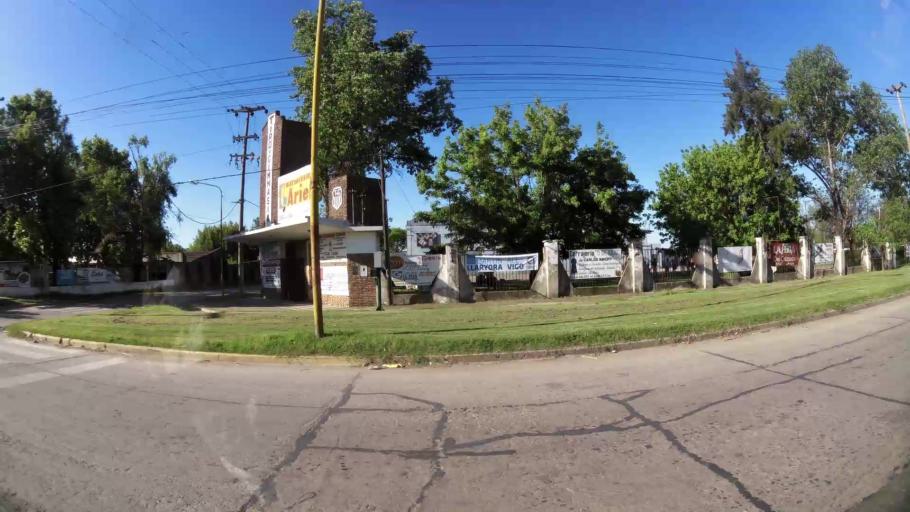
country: AR
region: Cordoba
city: San Francisco
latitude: -31.4171
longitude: -62.0805
